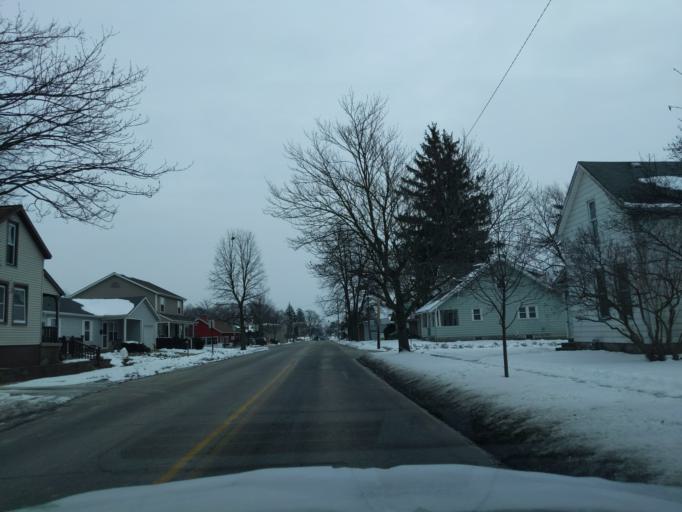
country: US
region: Indiana
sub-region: Tippecanoe County
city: Lafayette
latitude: 40.4100
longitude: -86.8806
